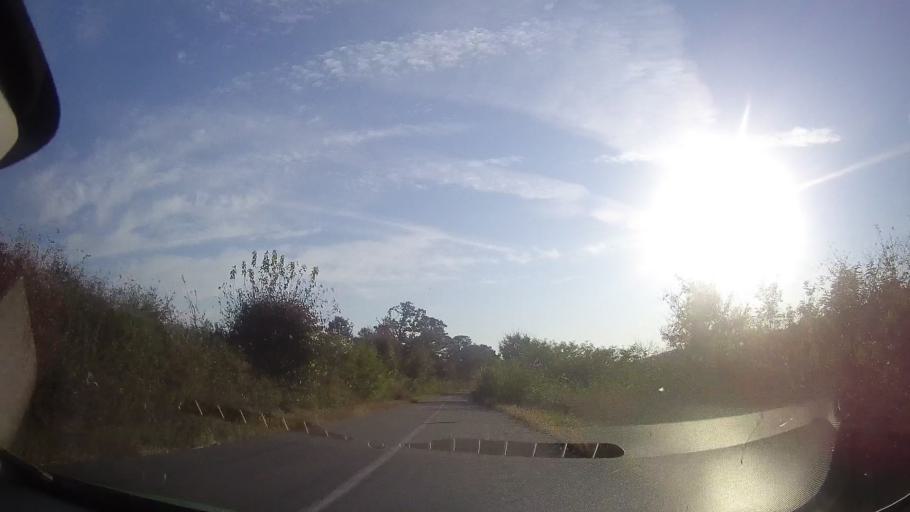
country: RO
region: Timis
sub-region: Comuna Bogda
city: Bogda
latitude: 45.9809
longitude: 21.5281
